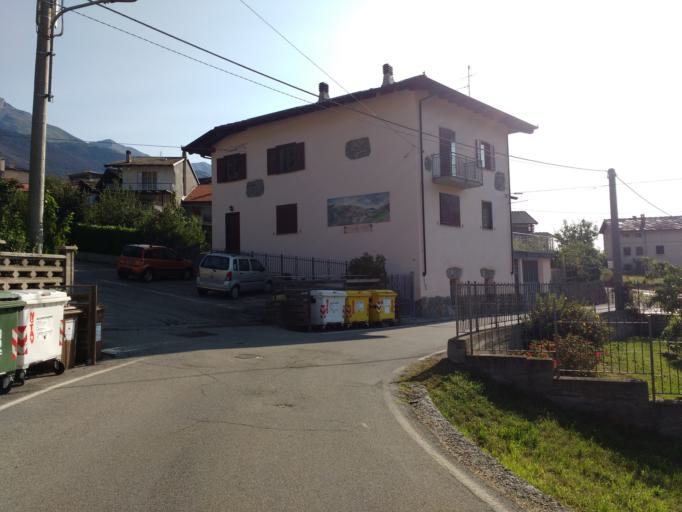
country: IT
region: Piedmont
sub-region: Provincia di Torino
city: Giaglione
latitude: 45.1423
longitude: 7.0116
